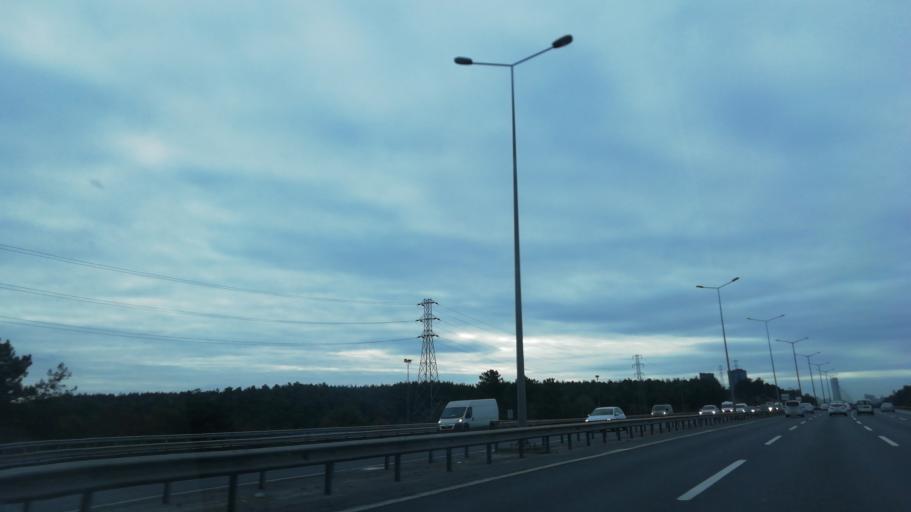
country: TR
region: Istanbul
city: Umraniye
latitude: 41.0473
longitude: 29.1213
